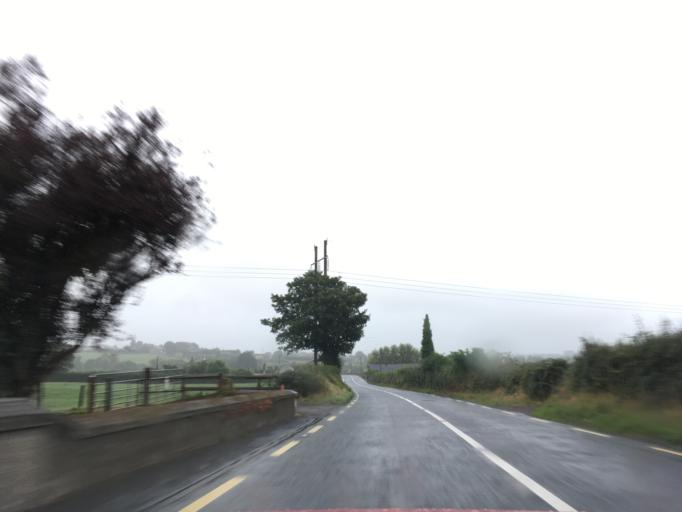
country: IE
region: Munster
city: Tipperary
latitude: 52.4836
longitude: -8.0757
